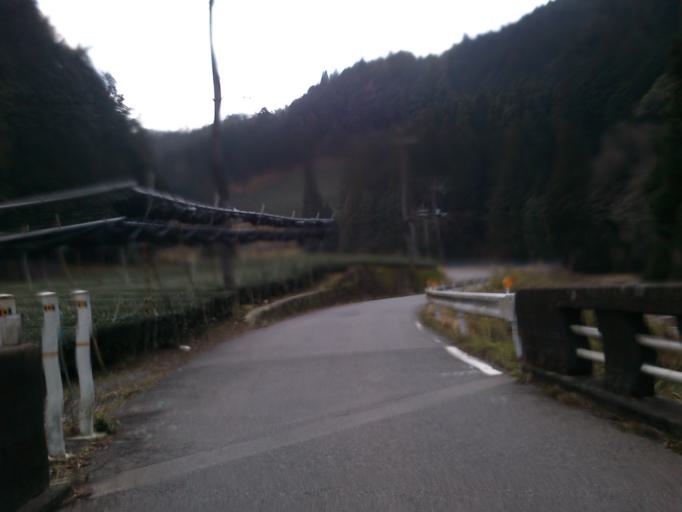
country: JP
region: Kyoto
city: Uji
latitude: 34.8267
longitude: 135.9648
